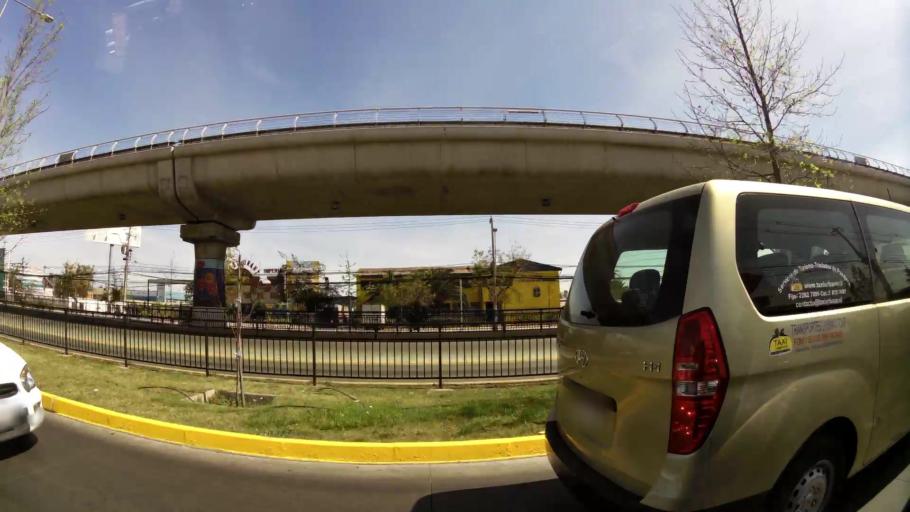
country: CL
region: Santiago Metropolitan
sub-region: Provincia de Cordillera
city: Puente Alto
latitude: -33.5821
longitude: -70.5811
